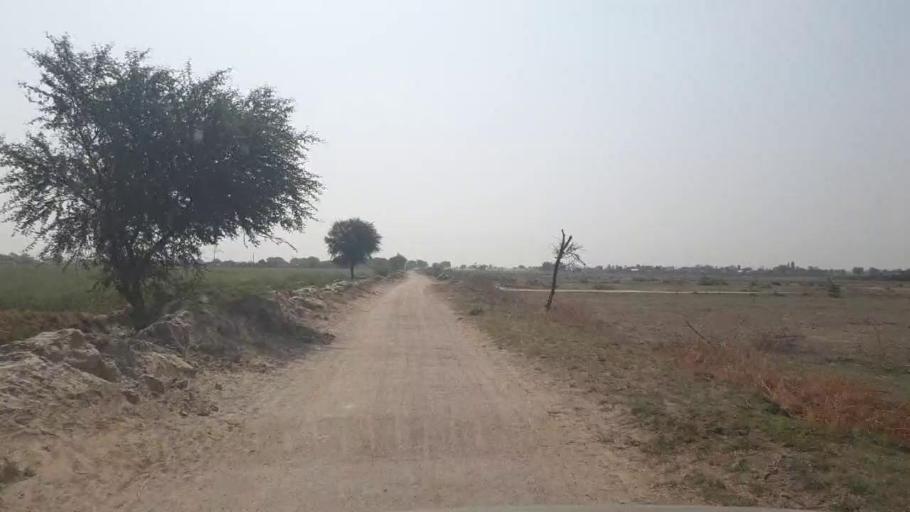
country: PK
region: Sindh
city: Dhoro Naro
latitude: 25.4416
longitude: 69.6260
